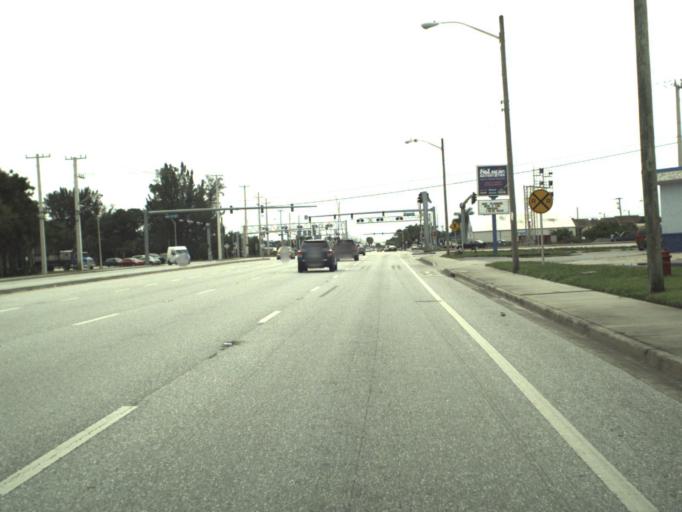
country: US
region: Florida
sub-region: Palm Beach County
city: Mangonia Park
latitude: 26.7811
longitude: -80.1075
